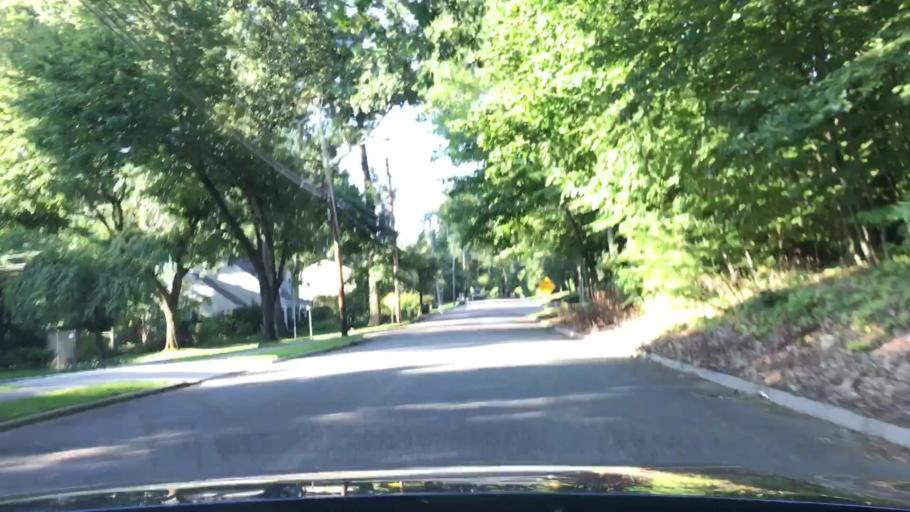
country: US
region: New Jersey
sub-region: Bergen County
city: Alpine
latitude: 40.9705
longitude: -73.9361
